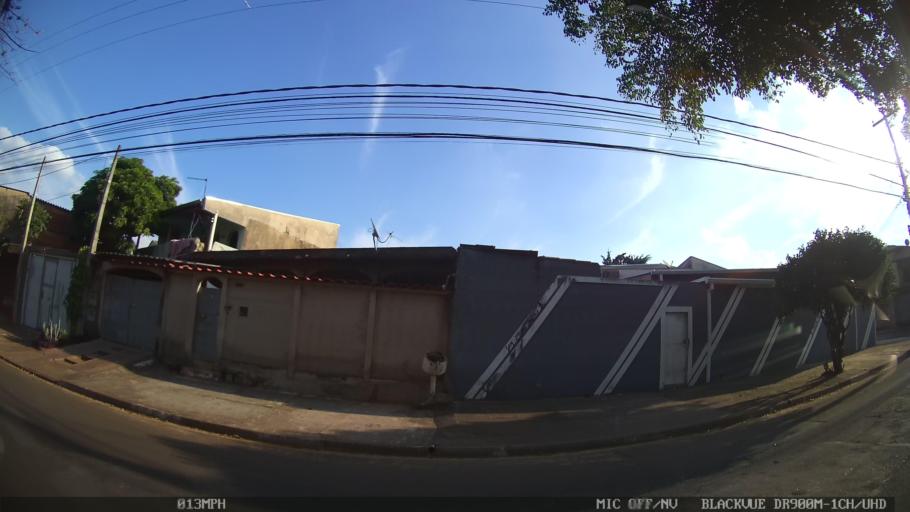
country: BR
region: Sao Paulo
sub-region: Hortolandia
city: Hortolandia
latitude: -22.8778
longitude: -47.1430
